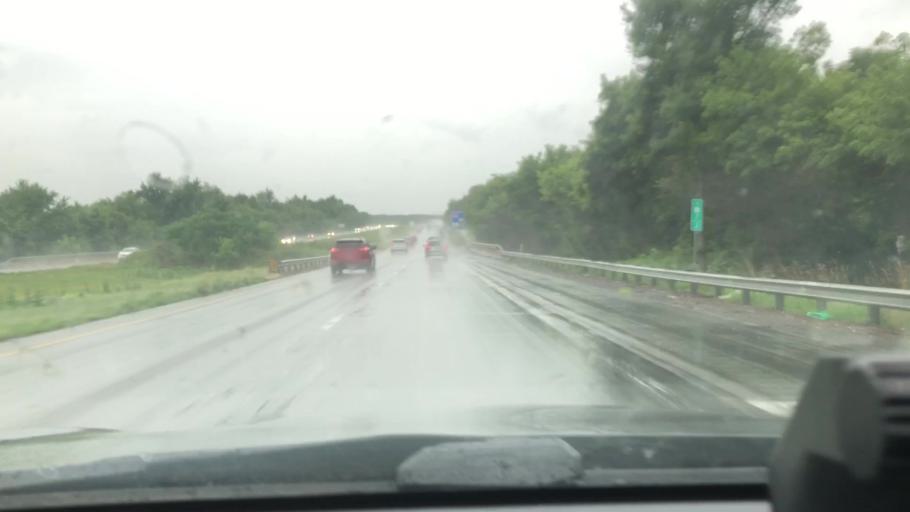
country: US
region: Pennsylvania
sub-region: Northampton County
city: Tatamy
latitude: 40.7252
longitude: -75.2786
